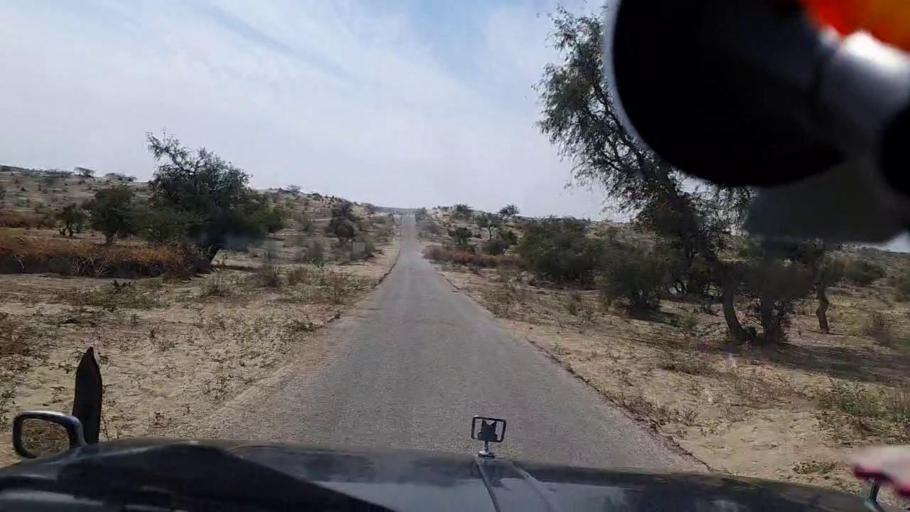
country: PK
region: Sindh
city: Diplo
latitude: 24.4202
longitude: 69.5835
